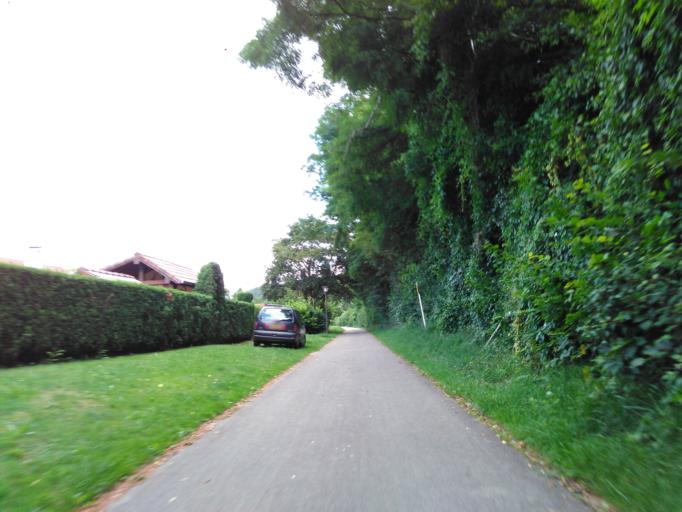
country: DE
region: Rheinland-Pfalz
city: Menningen
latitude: 49.8171
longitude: 6.4759
